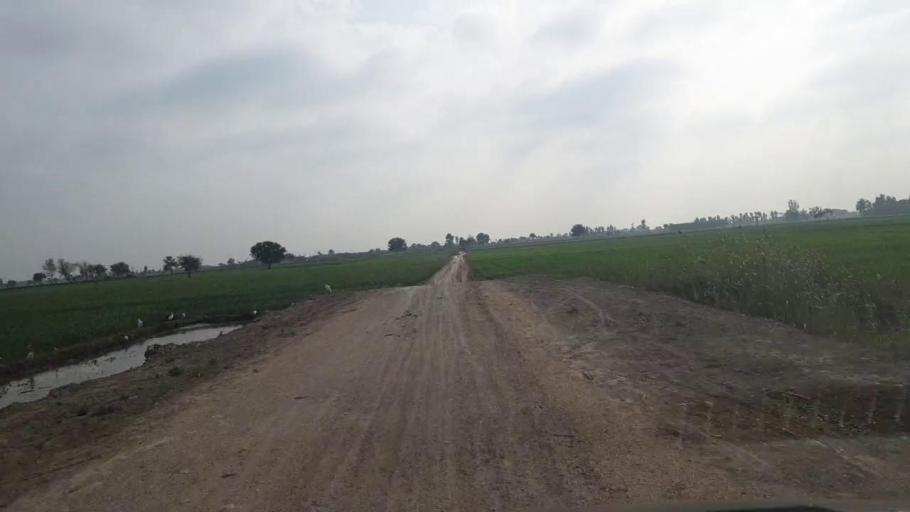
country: PK
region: Sindh
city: Shahdadpur
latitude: 25.8987
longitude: 68.6576
